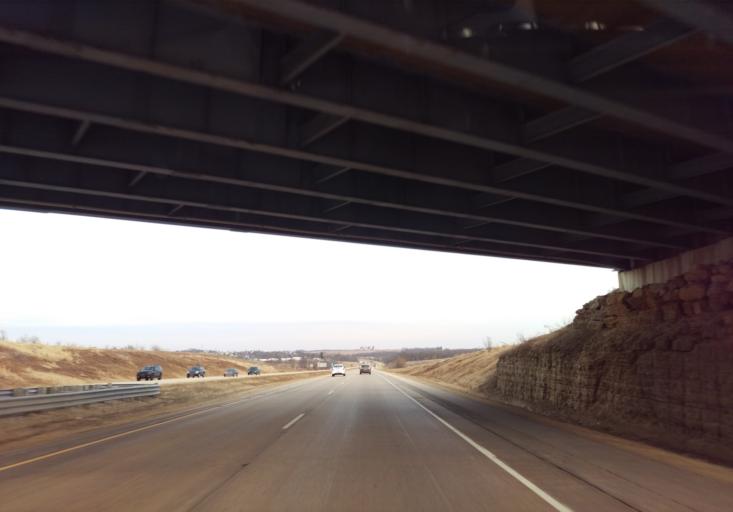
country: US
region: Wisconsin
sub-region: Dane County
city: Mount Horeb
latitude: 43.0010
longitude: -89.7604
